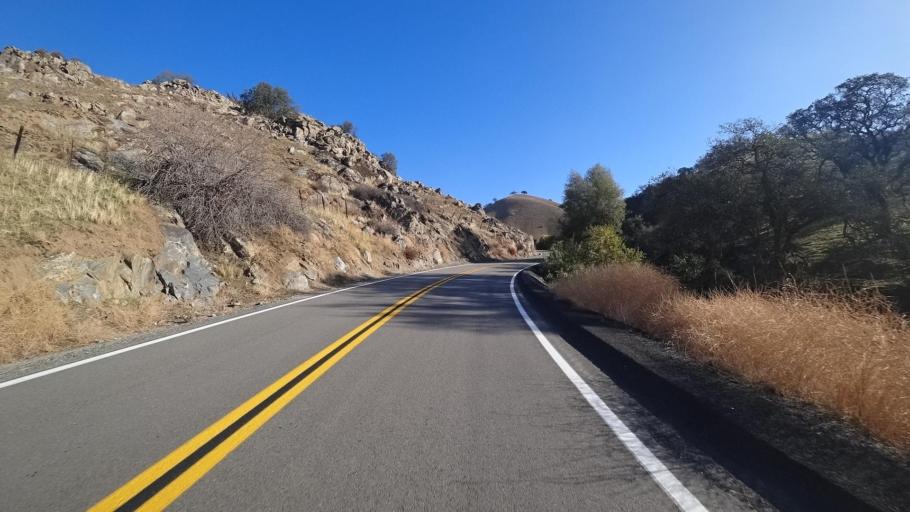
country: US
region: California
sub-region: Kern County
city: Alta Sierra
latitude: 35.7076
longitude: -118.8245
